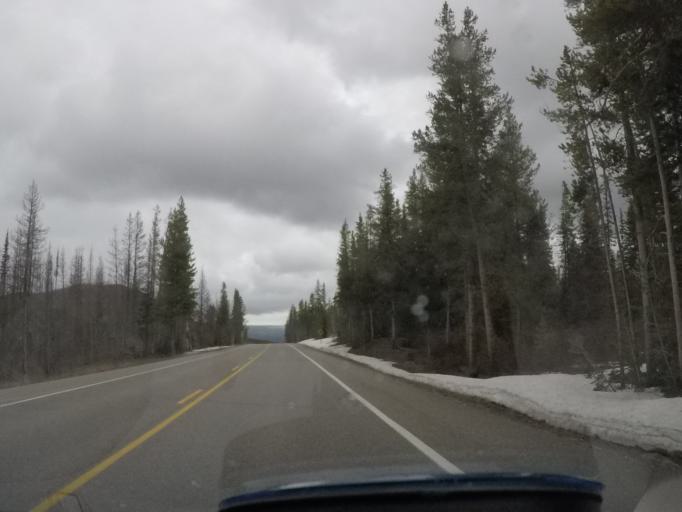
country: US
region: Idaho
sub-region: Teton County
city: Driggs
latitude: 44.0559
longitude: -110.6902
